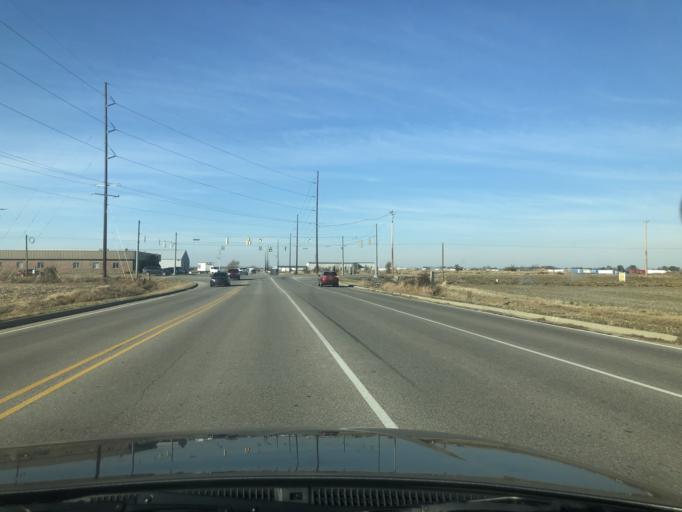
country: US
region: Indiana
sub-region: Warrick County
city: Newburgh
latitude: 37.9913
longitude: -87.4397
